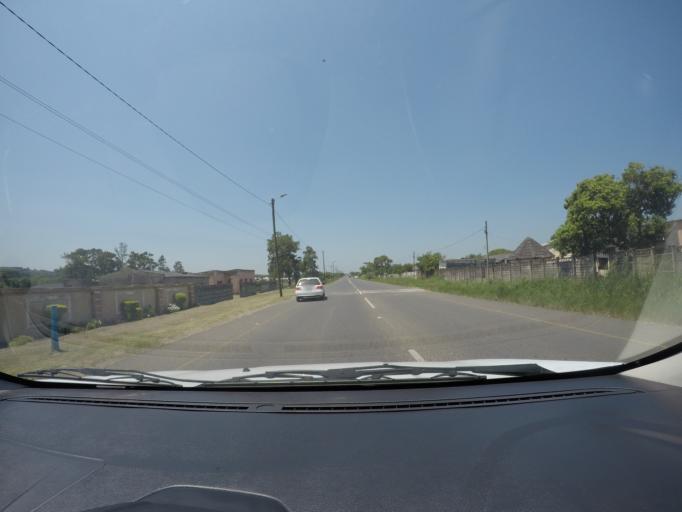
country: ZA
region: KwaZulu-Natal
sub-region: uThungulu District Municipality
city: eSikhawini
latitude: -28.8801
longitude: 31.8909
